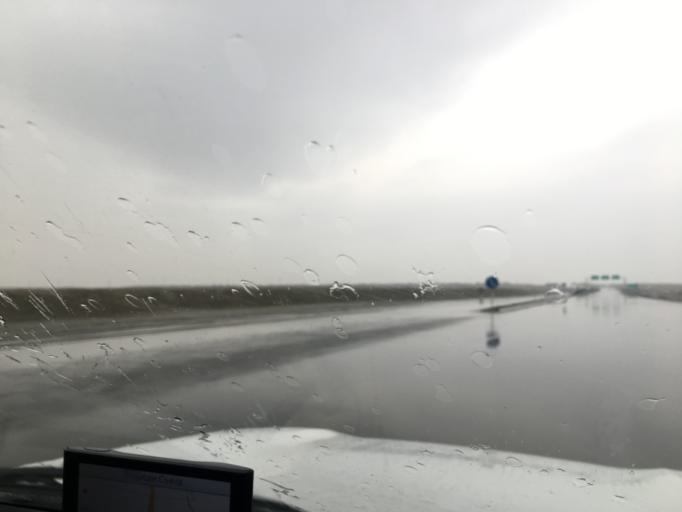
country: TM
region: Ahal
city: Annau
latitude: 37.8430
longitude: 58.7181
